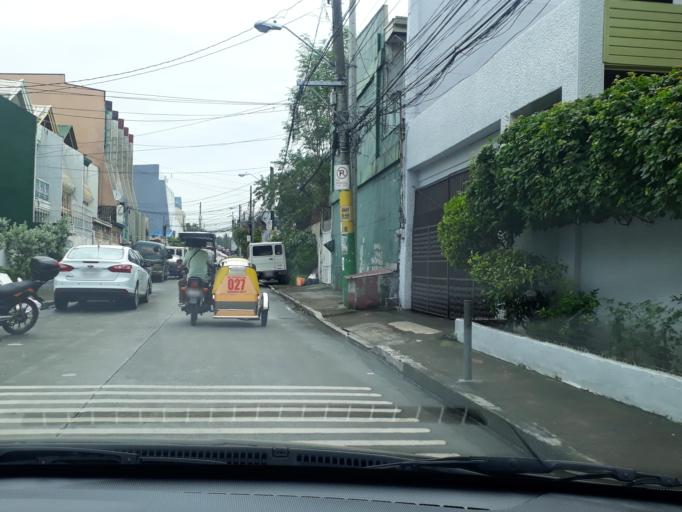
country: PH
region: Metro Manila
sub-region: Quezon City
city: Quezon City
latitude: 14.6301
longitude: 121.0489
